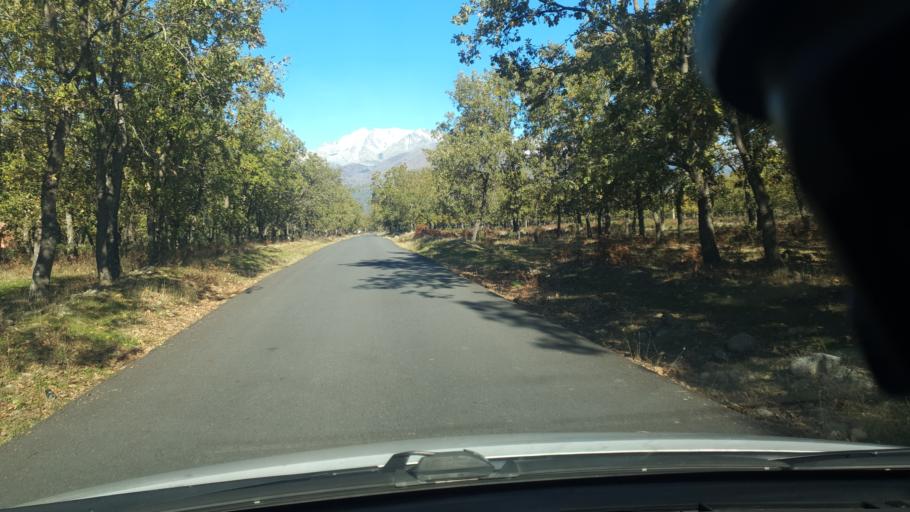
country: ES
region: Castille and Leon
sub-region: Provincia de Avila
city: Candeleda
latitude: 40.1234
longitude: -5.2664
